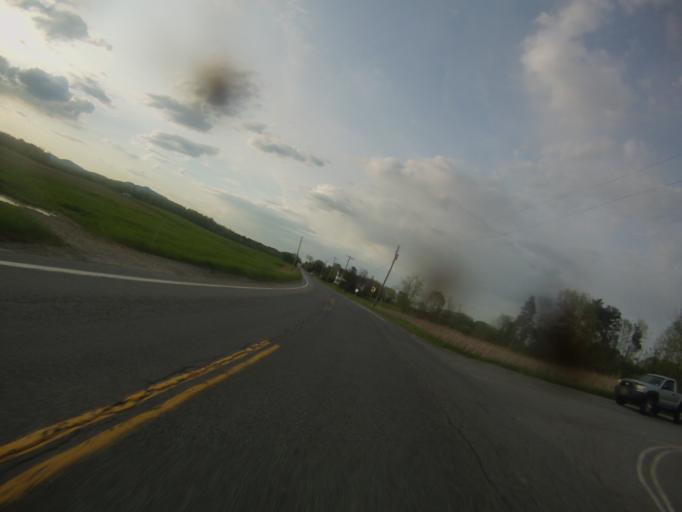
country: US
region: New York
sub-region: Essex County
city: Port Henry
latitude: 44.0013
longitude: -73.4200
